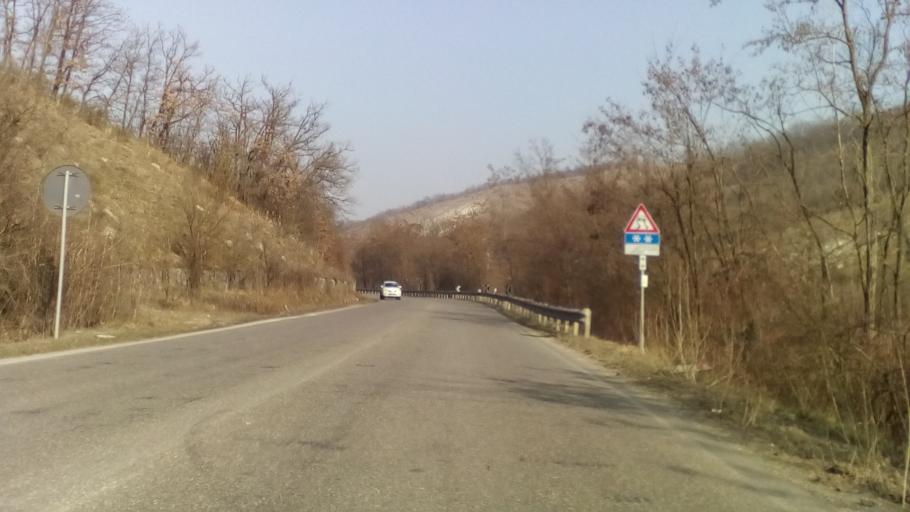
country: IT
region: Emilia-Romagna
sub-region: Provincia di Modena
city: Serramazzoni
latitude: 44.4626
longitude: 10.8358
